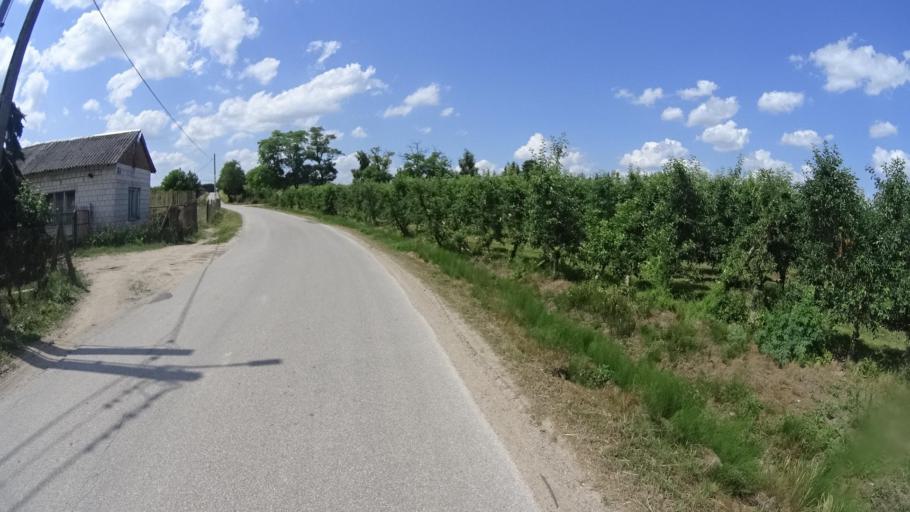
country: PL
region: Masovian Voivodeship
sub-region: Powiat grojecki
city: Goszczyn
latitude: 51.7258
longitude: 20.8459
